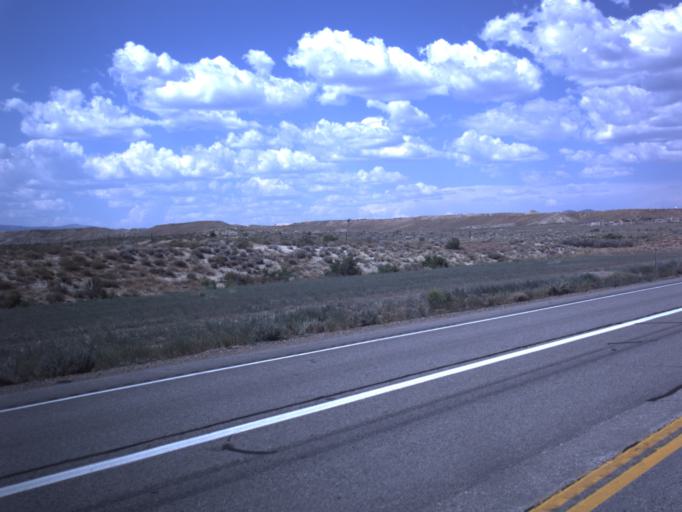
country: US
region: Utah
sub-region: Carbon County
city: Price
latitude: 39.5257
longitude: -110.8225
